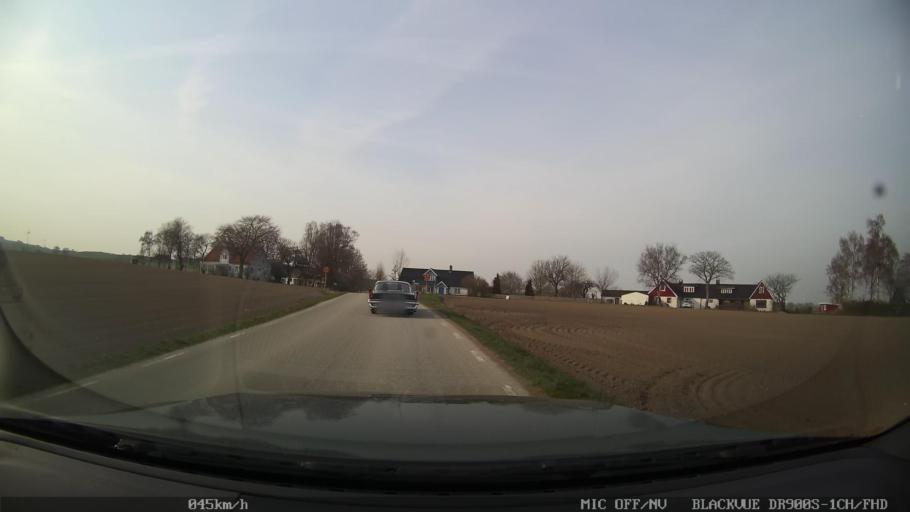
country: SE
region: Skane
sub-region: Ystads Kommun
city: Ystad
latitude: 55.4626
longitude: 13.8241
